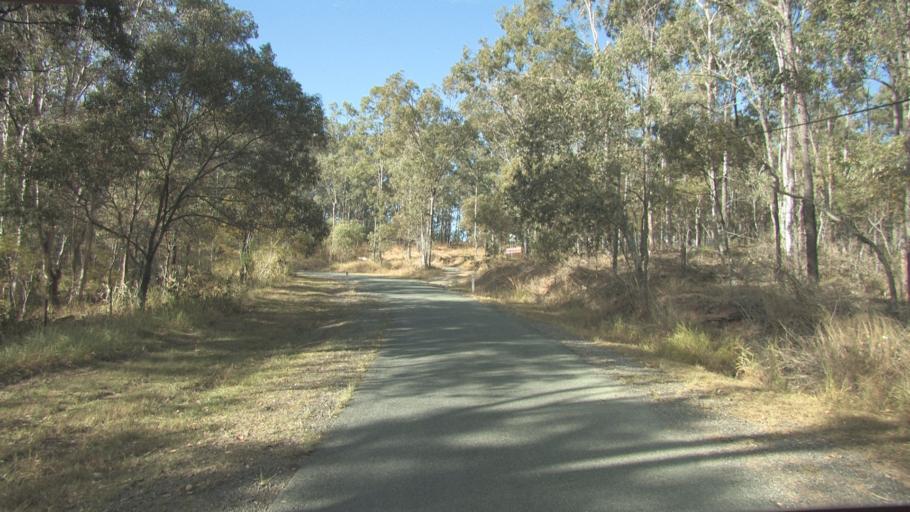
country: AU
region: Queensland
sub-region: Logan
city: Cedar Vale
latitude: -27.8488
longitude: 153.0726
